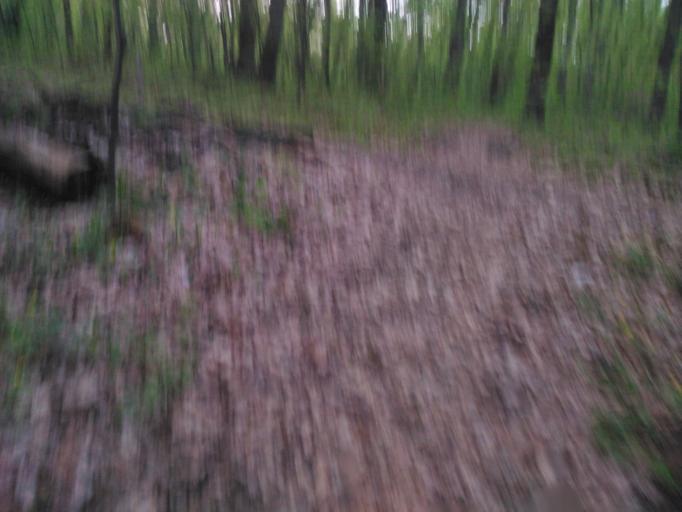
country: RU
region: Ulyanovsk
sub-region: Ulyanovskiy Rayon
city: Ulyanovsk
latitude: 54.2720
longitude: 48.3387
